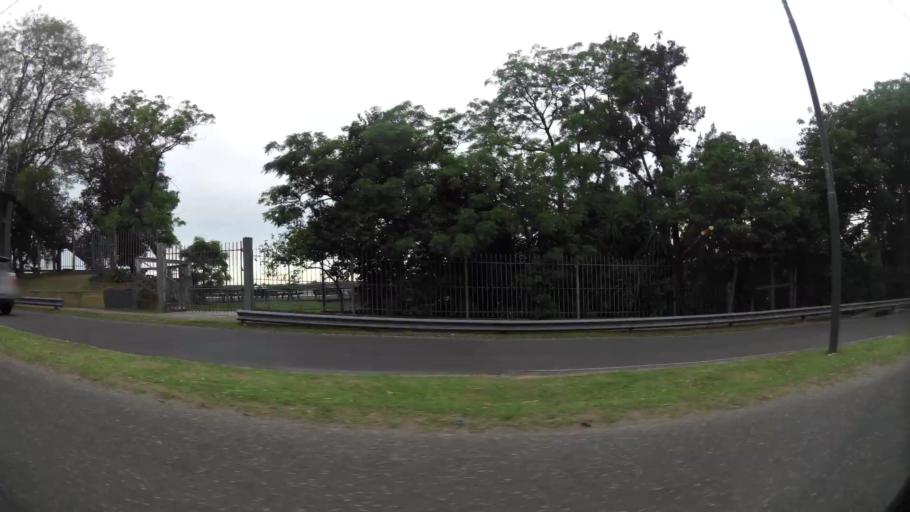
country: AR
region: Santa Fe
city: Granadero Baigorria
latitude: -32.8791
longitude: -60.6878
